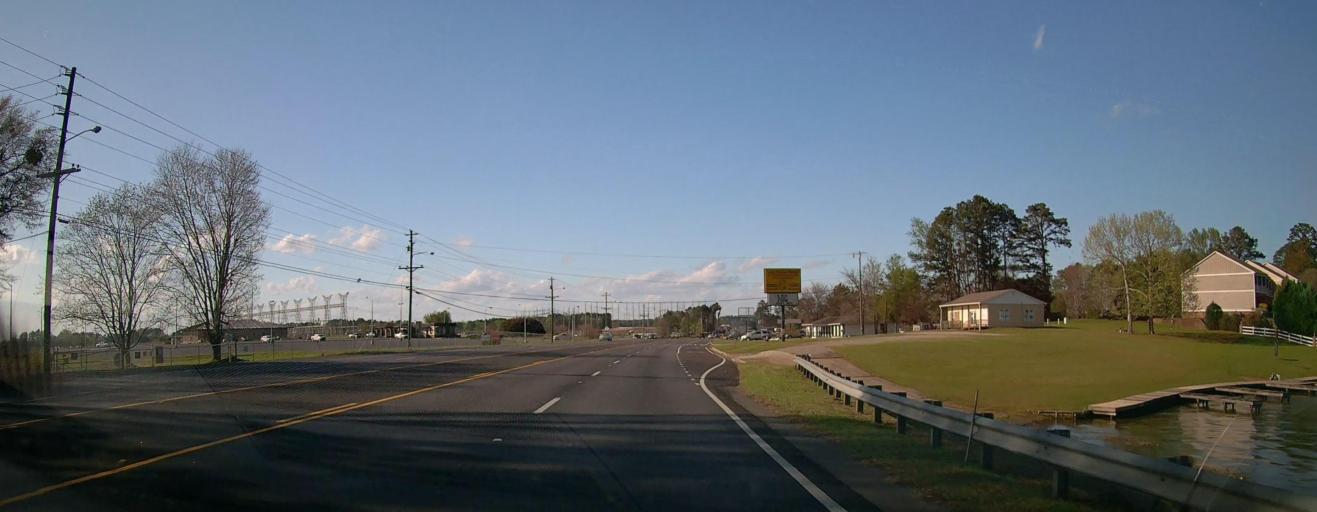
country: US
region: Georgia
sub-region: Baldwin County
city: Milledgeville
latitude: 33.1926
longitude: -83.2940
